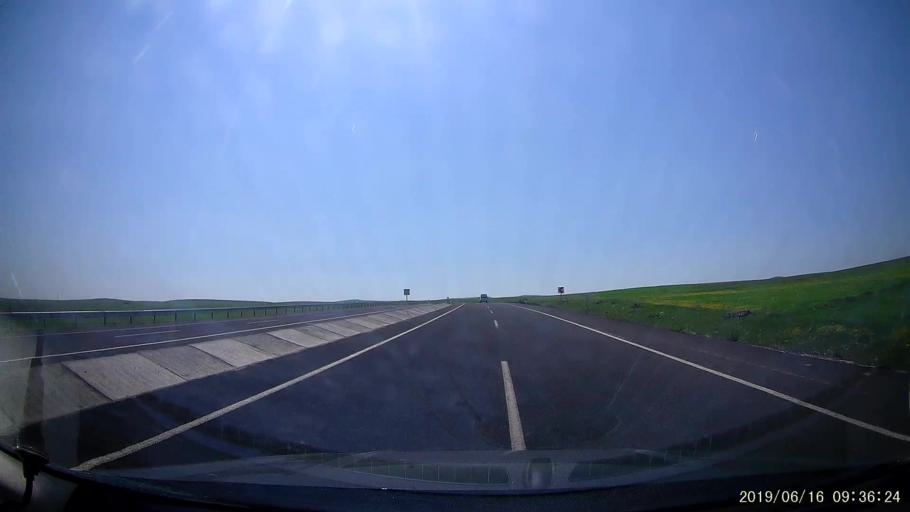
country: TR
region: Kars
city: Kars
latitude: 40.5583
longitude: 43.1717
